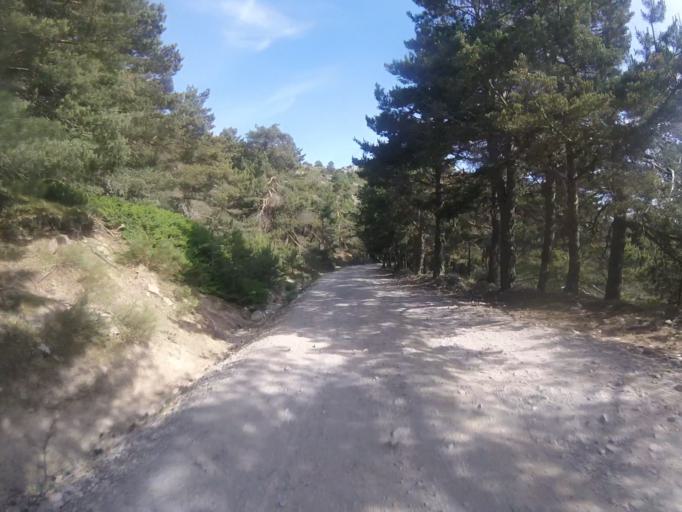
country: ES
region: Madrid
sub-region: Provincia de Madrid
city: Guadarrama
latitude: 40.6886
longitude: -4.1540
